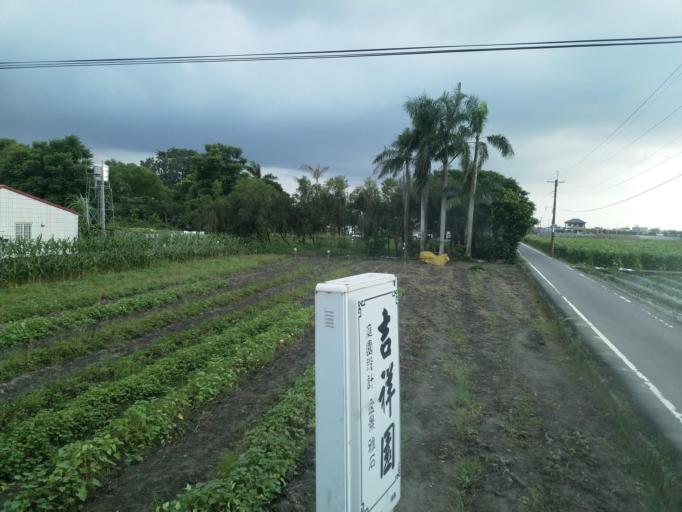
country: TW
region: Taiwan
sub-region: Pingtung
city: Pingtung
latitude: 22.8657
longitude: 120.5422
